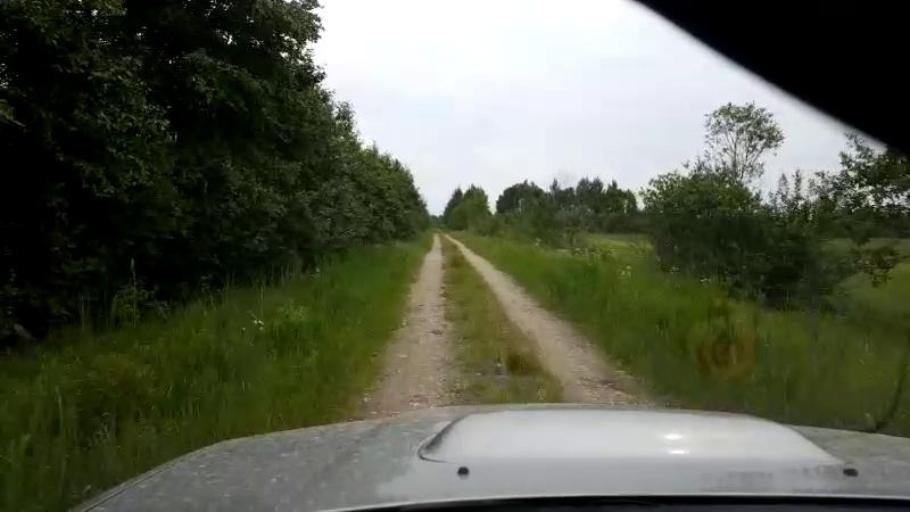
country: EE
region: Paernumaa
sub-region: Tootsi vald
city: Tootsi
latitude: 58.5614
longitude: 24.6885
